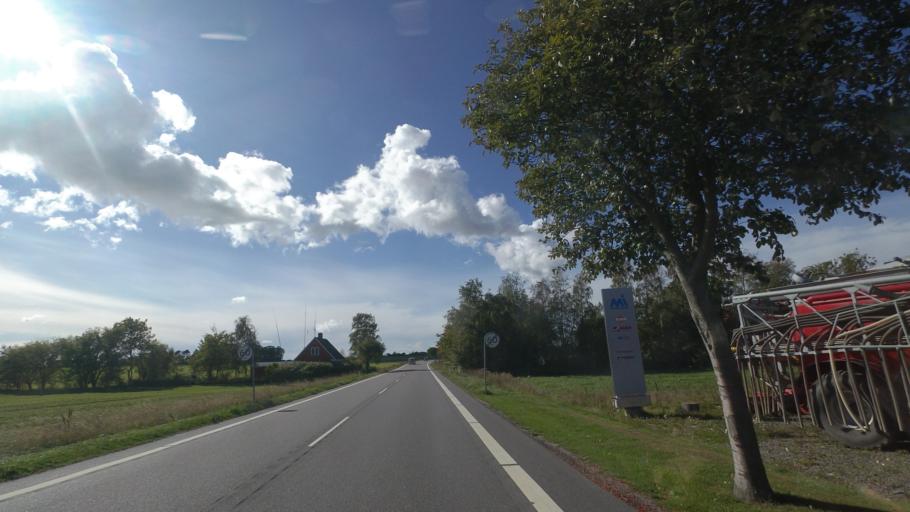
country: DK
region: Capital Region
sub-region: Bornholm Kommune
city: Akirkeby
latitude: 55.0707
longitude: 14.8280
